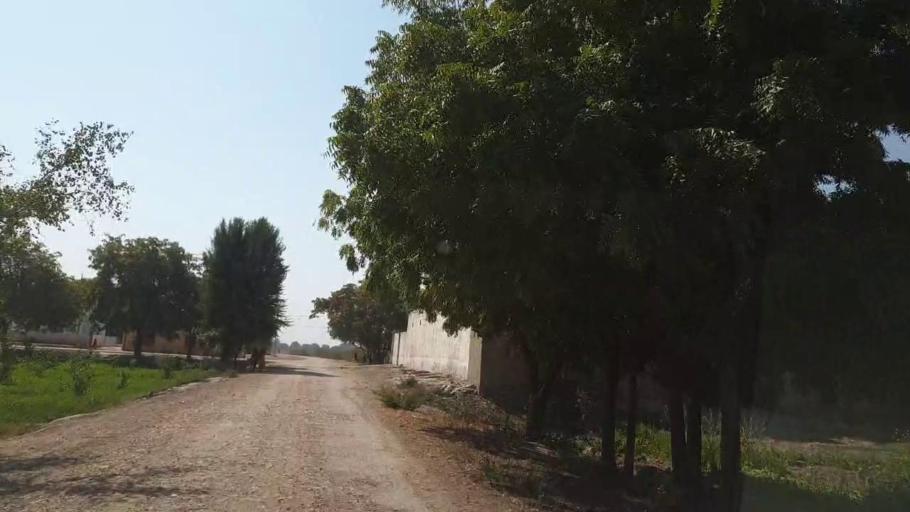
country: PK
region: Sindh
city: Kunri
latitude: 25.1695
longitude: 69.5302
